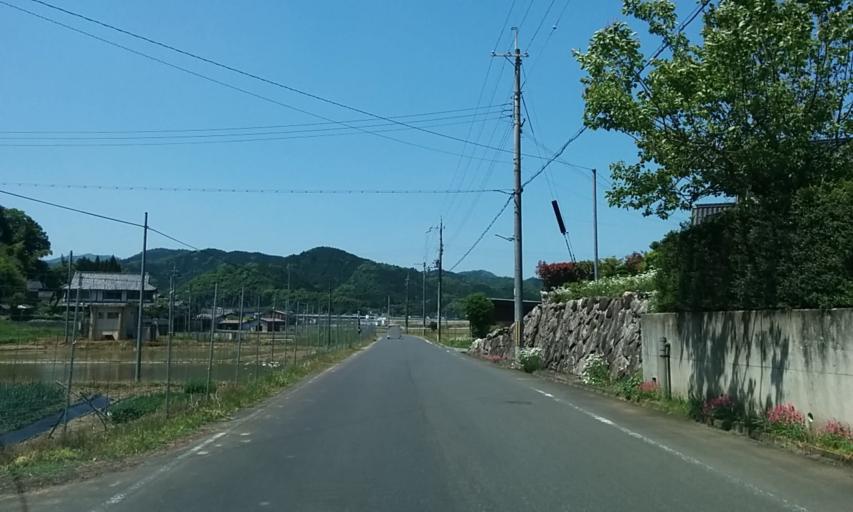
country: JP
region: Kyoto
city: Ayabe
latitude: 35.3849
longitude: 135.1841
